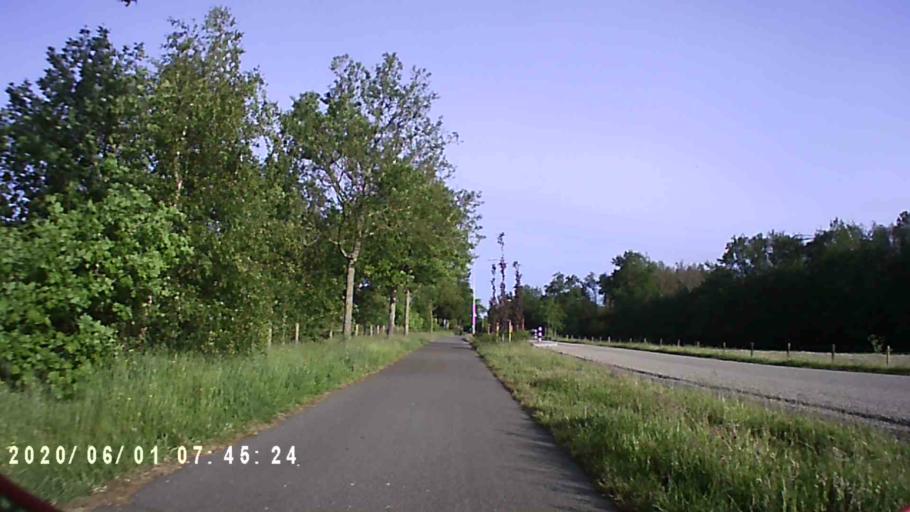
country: NL
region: Friesland
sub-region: Gemeente Dantumadiel
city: Rinsumageast
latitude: 53.2931
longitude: 5.9627
